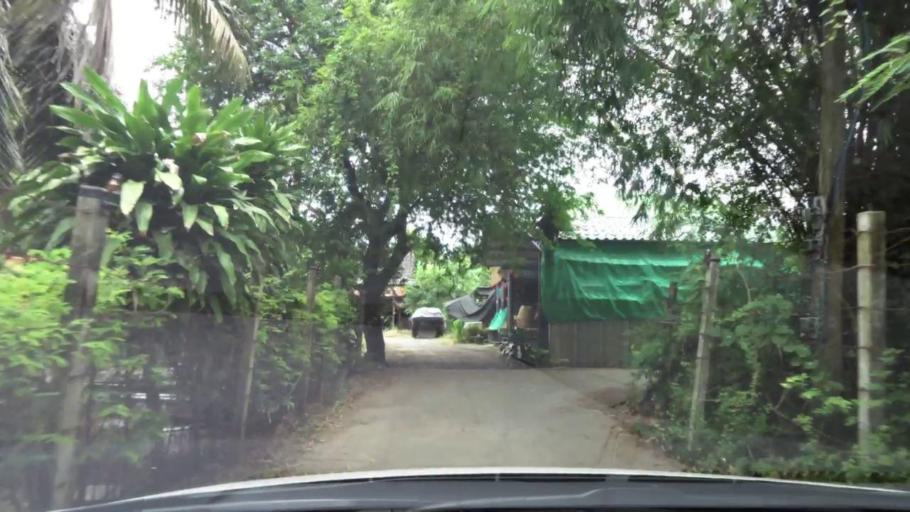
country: TH
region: Samut Sakhon
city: Ban Phaeo
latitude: 13.6241
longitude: 100.0264
